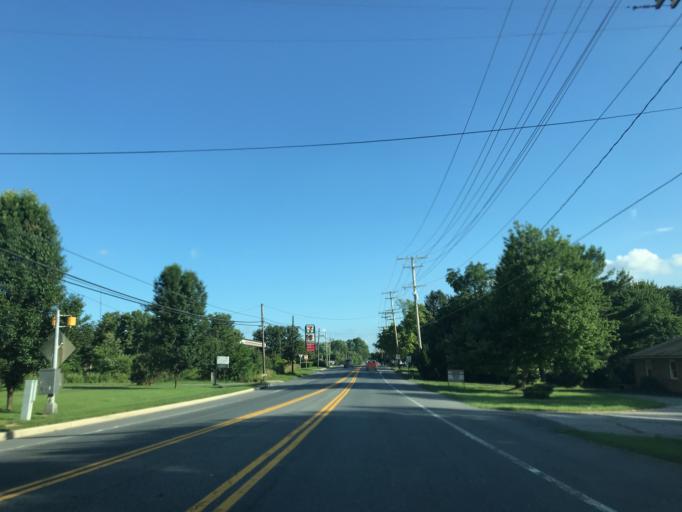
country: US
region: Maryland
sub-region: Carroll County
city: Hampstead
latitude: 39.5790
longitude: -76.8408
